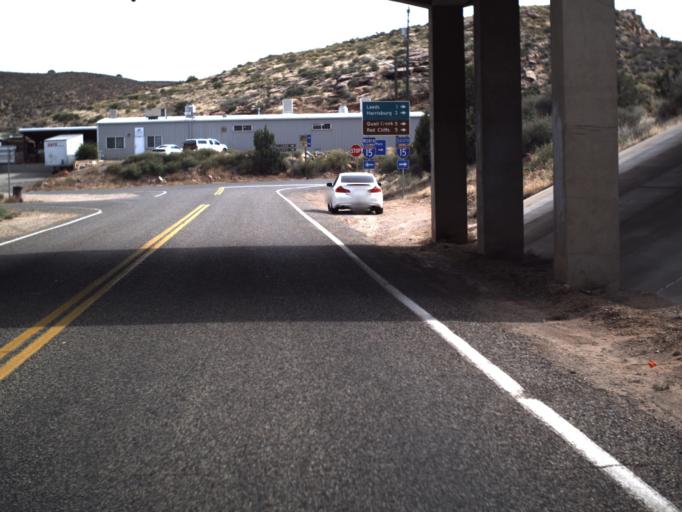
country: US
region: Utah
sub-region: Washington County
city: Toquerville
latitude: 37.2442
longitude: -113.3532
